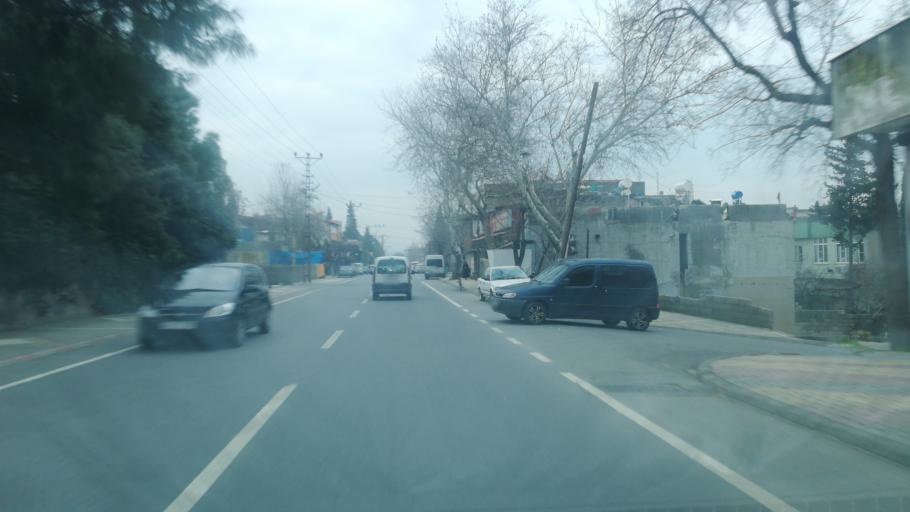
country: TR
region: Kahramanmaras
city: Kahramanmaras
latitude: 37.5714
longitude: 36.9477
